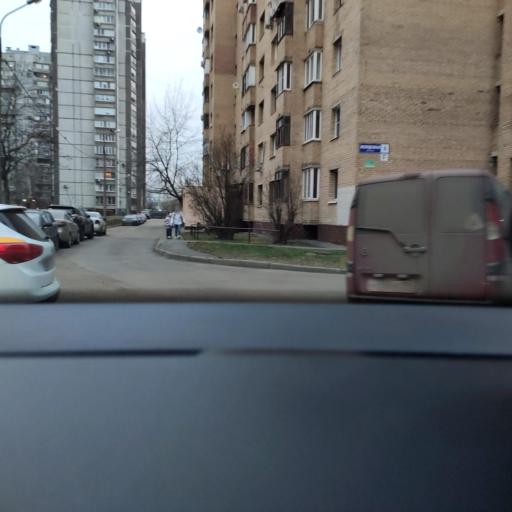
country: RU
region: Moskovskaya
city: Reutov
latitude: 55.7471
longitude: 37.8496
